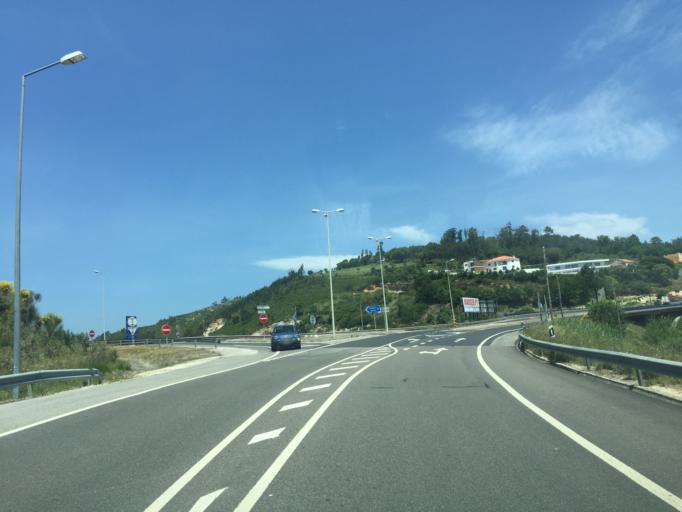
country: PT
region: Lisbon
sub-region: Mafra
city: Venda do Pinheiro
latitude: 38.9014
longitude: -9.2047
